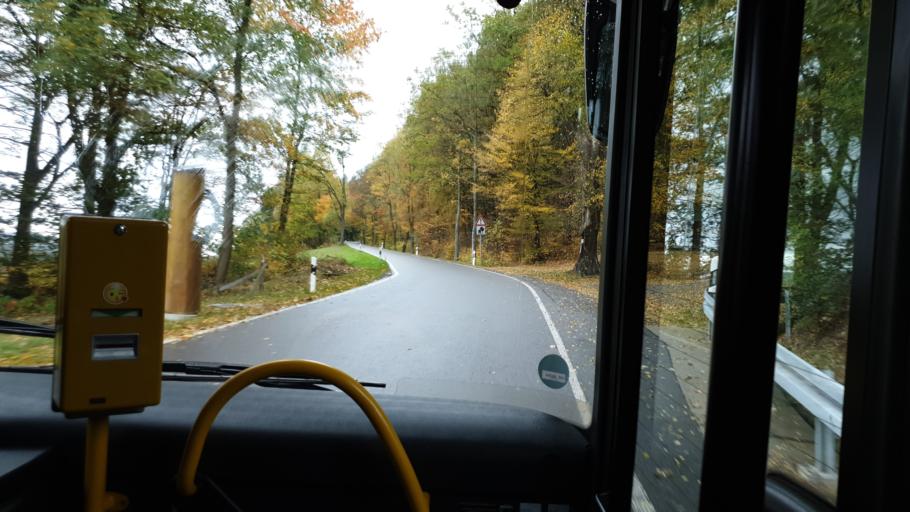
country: DE
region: Saxony
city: Kurort Gohrisch
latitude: 50.8883
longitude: 14.1119
